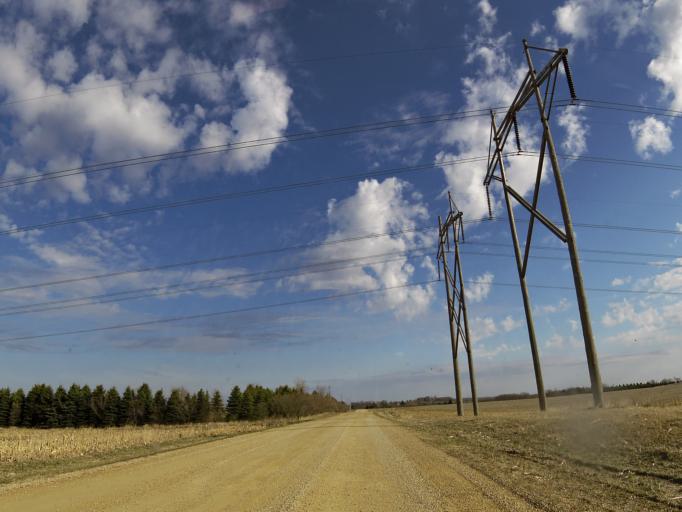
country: US
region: Minnesota
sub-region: Dakota County
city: Hastings
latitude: 44.8145
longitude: -92.8417
